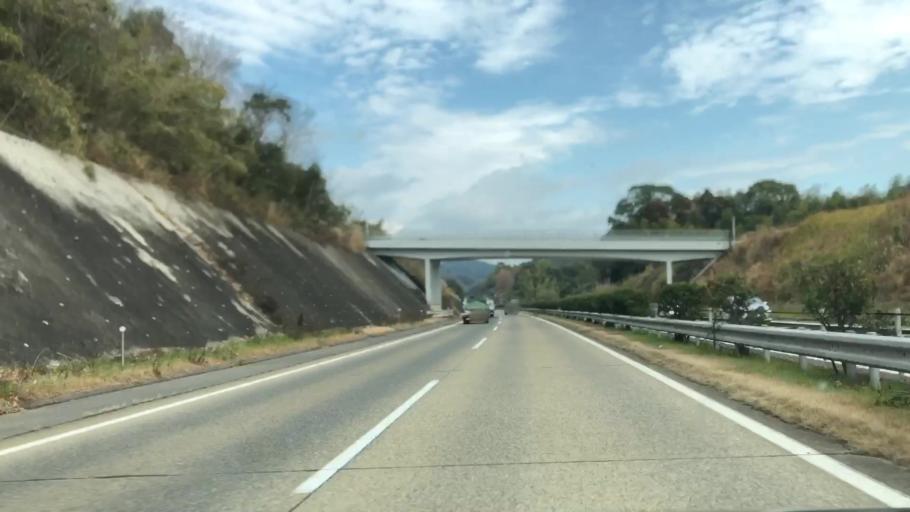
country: JP
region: Saga Prefecture
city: Kanzakimachi-kanzaki
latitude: 33.3314
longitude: 130.3194
